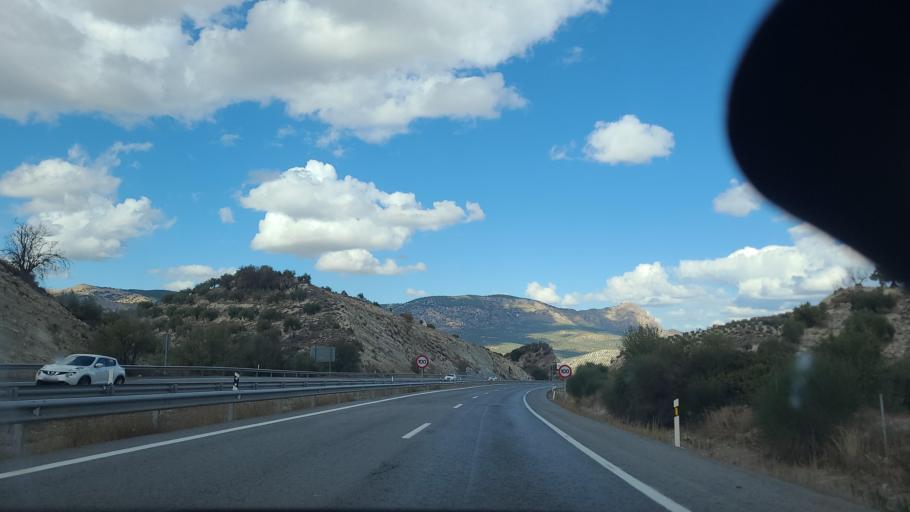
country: ES
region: Andalusia
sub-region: Provincia de Jaen
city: Campillo de Arenas
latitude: 37.5379
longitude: -3.6358
